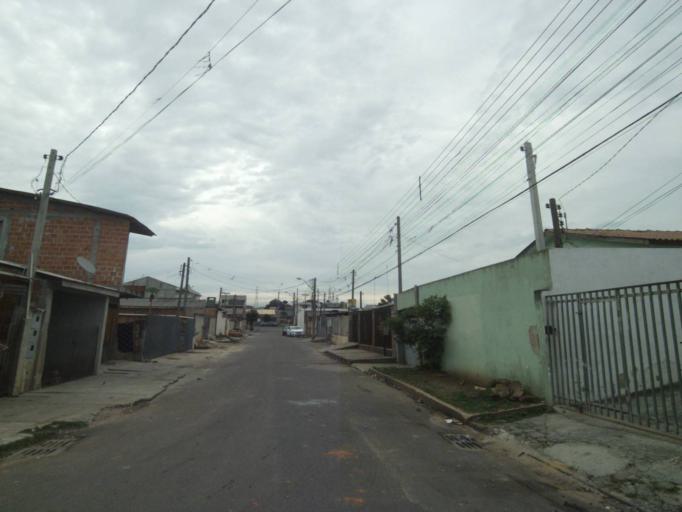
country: BR
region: Parana
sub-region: Curitiba
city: Curitiba
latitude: -25.4993
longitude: -49.3370
